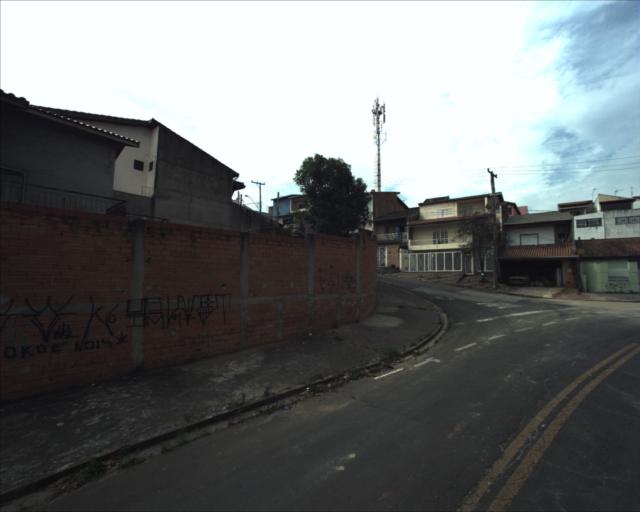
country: BR
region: Sao Paulo
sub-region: Sorocaba
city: Sorocaba
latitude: -23.4636
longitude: -47.4358
